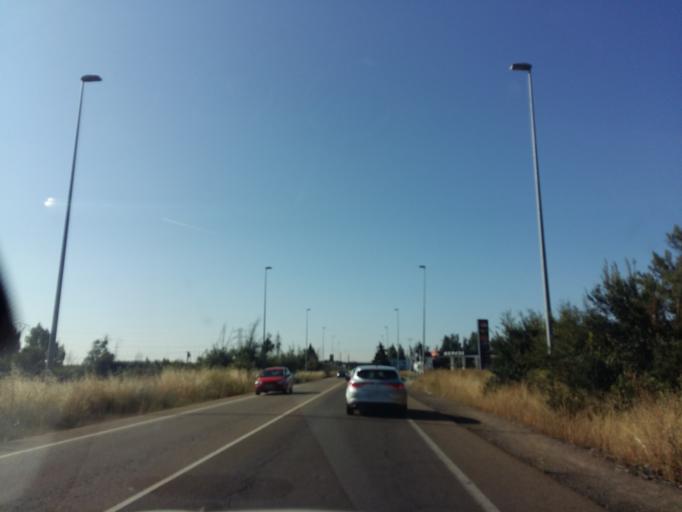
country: ES
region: Castille and Leon
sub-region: Provincia de Leon
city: Leon
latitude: 42.5736
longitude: -5.5831
